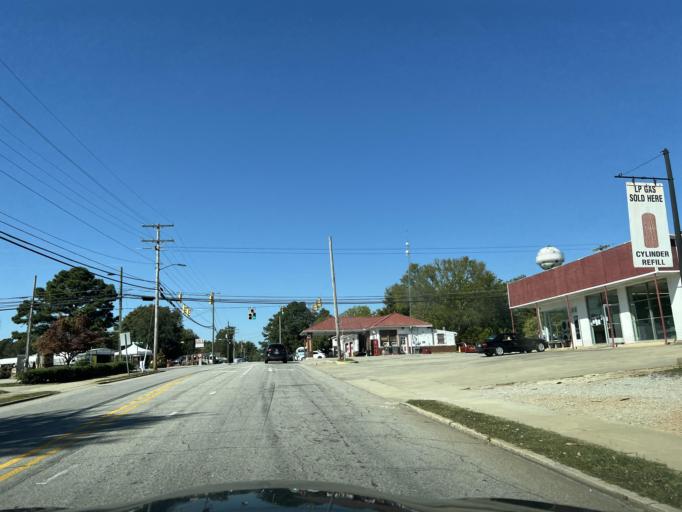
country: US
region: North Carolina
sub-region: Johnston County
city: Clayton
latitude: 35.6554
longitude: -78.4626
